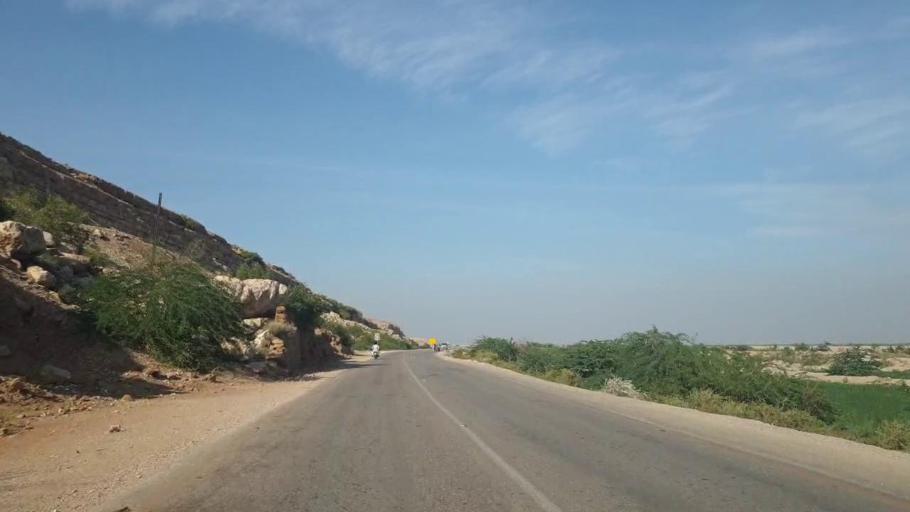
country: PK
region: Sindh
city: Sehwan
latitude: 26.3653
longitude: 67.8737
